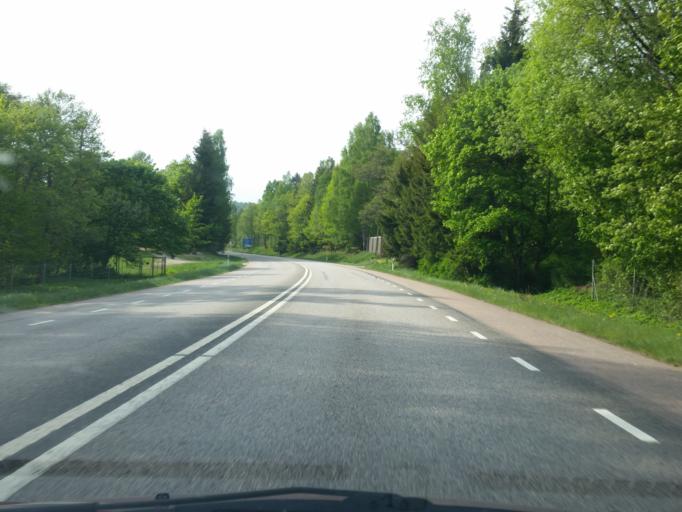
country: SE
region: Vaestra Goetaland
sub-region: Ulricehamns Kommun
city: Ulricehamn
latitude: 57.8113
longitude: 13.2955
